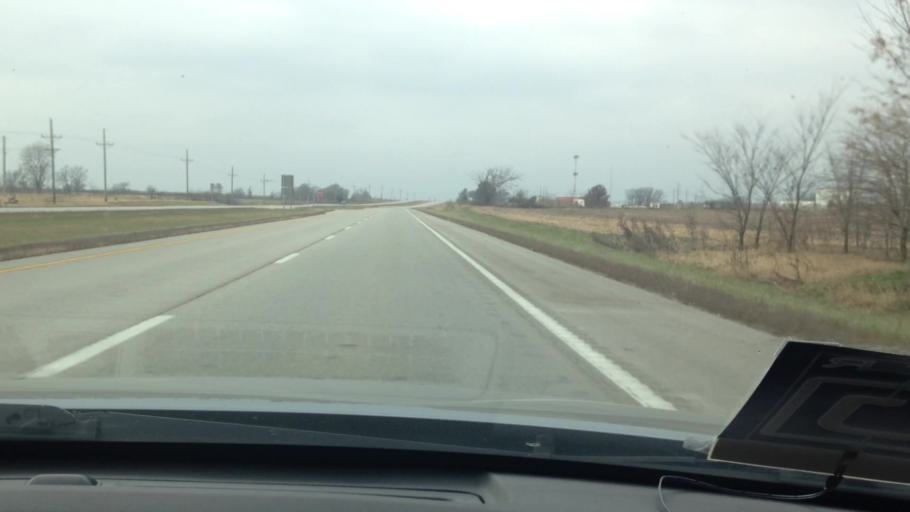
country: US
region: Missouri
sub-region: Cass County
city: Garden City
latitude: 38.5818
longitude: -94.2180
